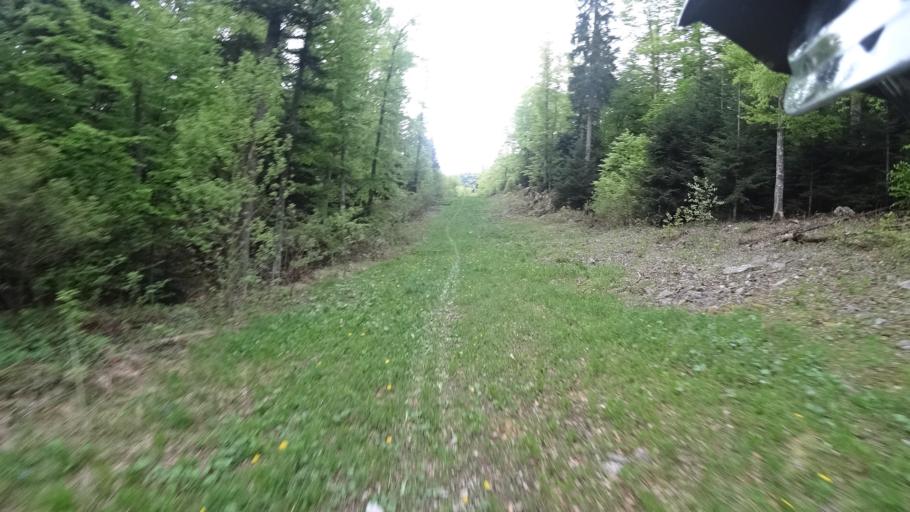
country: HR
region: Karlovacka
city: Plaski
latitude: 44.9278
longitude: 15.4253
